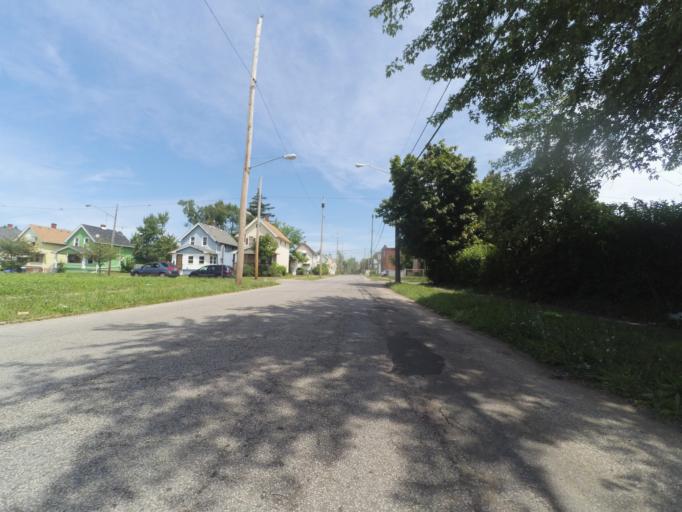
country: US
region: Ohio
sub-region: Cuyahoga County
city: Garfield Heights
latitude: 41.4592
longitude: -81.6128
